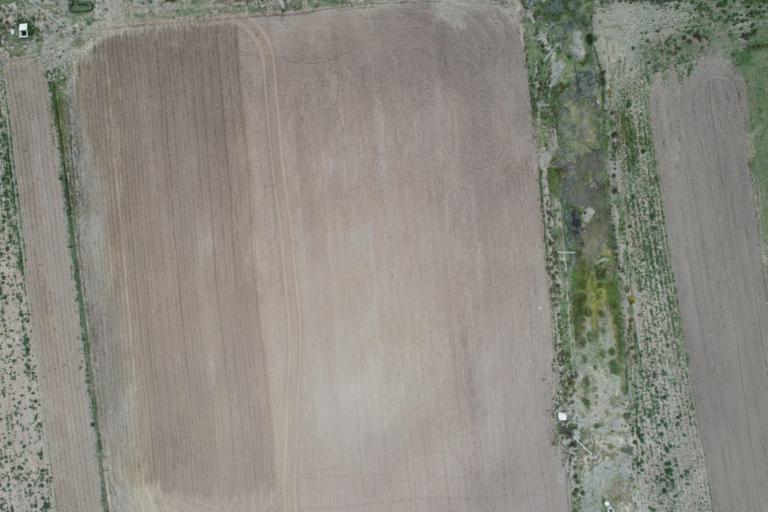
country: BO
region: La Paz
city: La Paz
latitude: -16.5167
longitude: -68.3016
